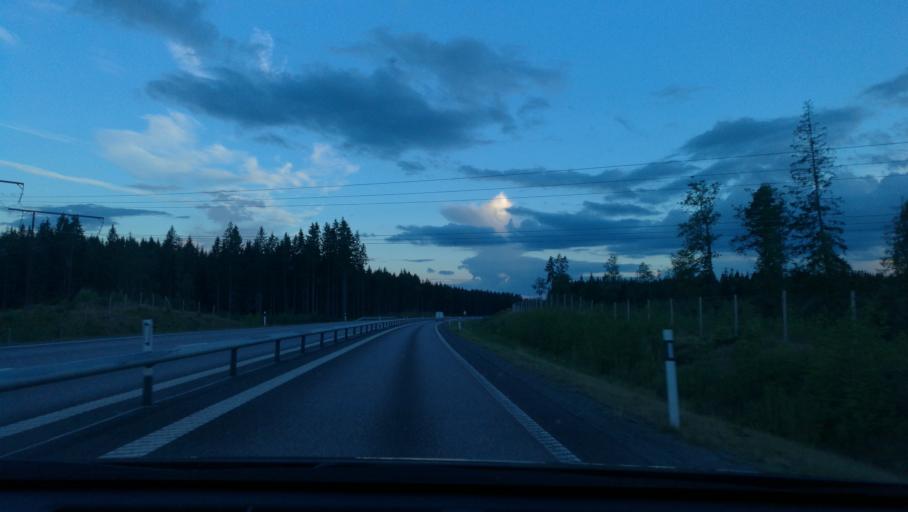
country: SE
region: Soedermanland
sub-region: Katrineholms Kommun
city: Katrineholm
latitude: 58.9474
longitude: 16.2167
